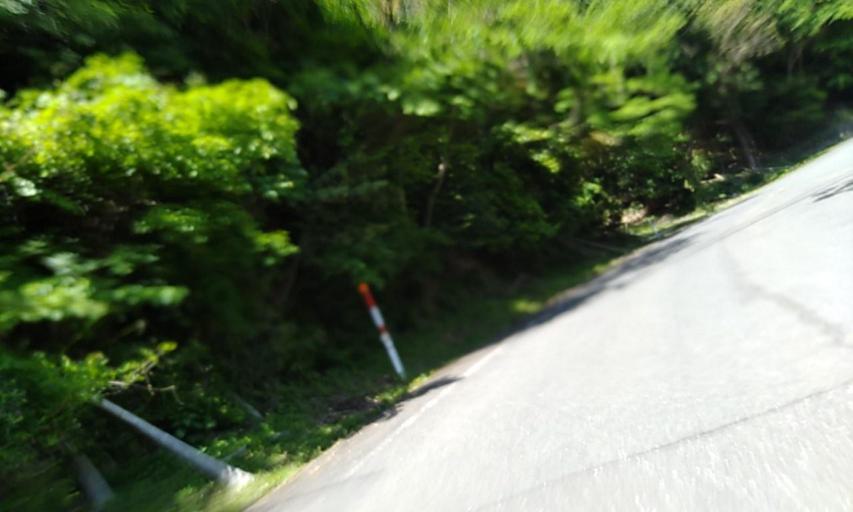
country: JP
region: Fukui
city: Obama
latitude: 35.5405
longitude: 135.7565
